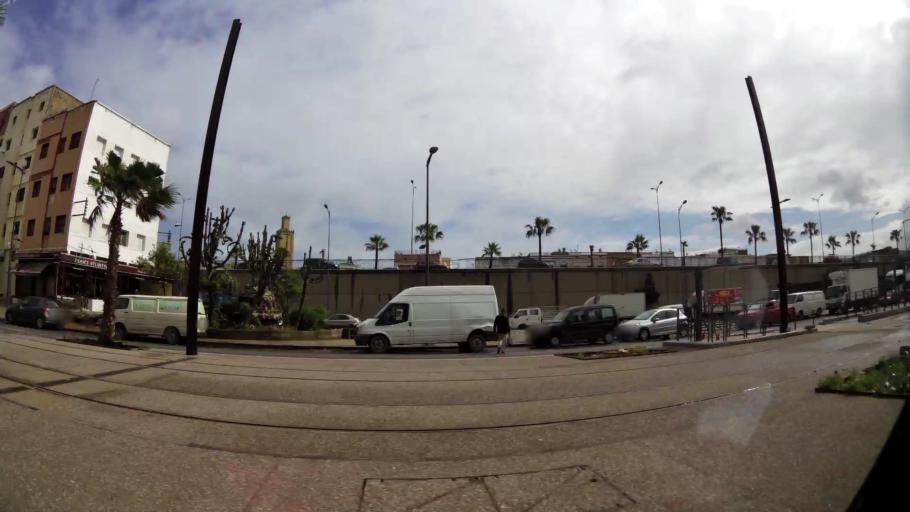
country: MA
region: Grand Casablanca
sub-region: Casablanca
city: Casablanca
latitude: 33.5728
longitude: -7.5813
